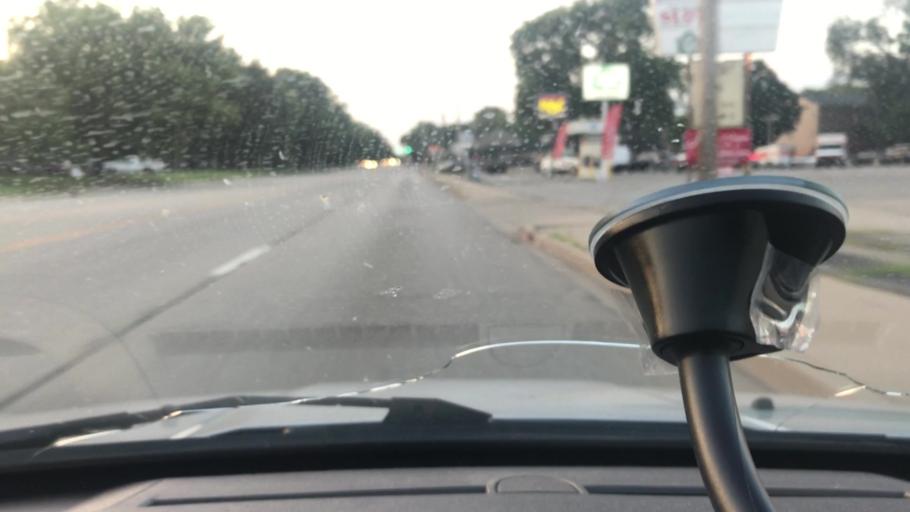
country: US
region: Illinois
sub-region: Tazewell County
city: Pekin
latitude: 40.5791
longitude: -89.6410
